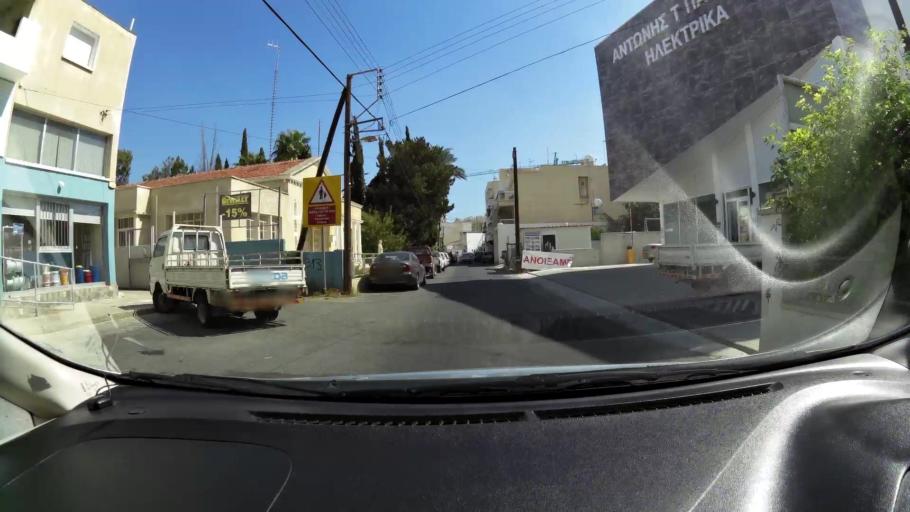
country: CY
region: Larnaka
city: Larnaca
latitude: 34.9151
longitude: 33.6322
